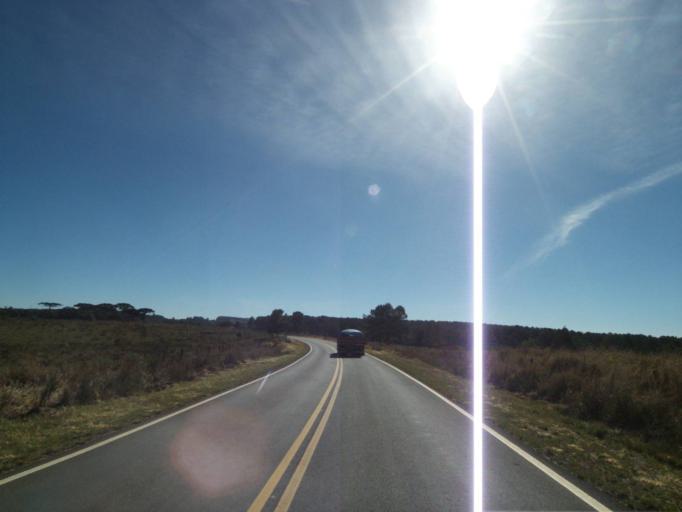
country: BR
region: Parana
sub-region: Castro
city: Castro
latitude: -24.7326
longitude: -50.1815
